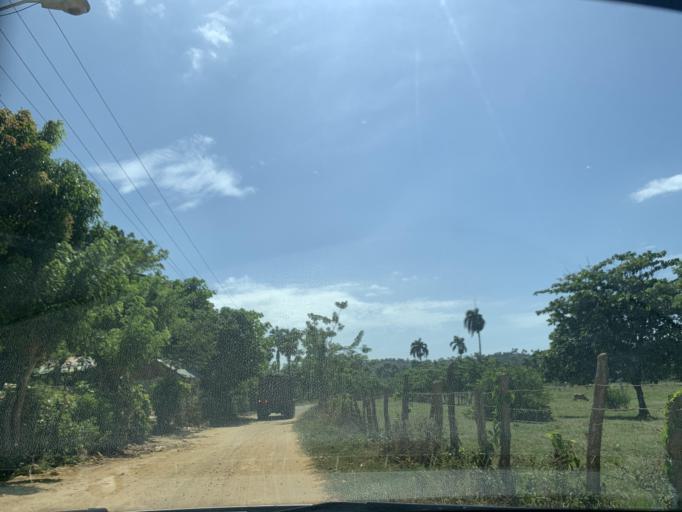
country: DO
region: Puerto Plata
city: Luperon
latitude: 19.8897
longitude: -70.8778
